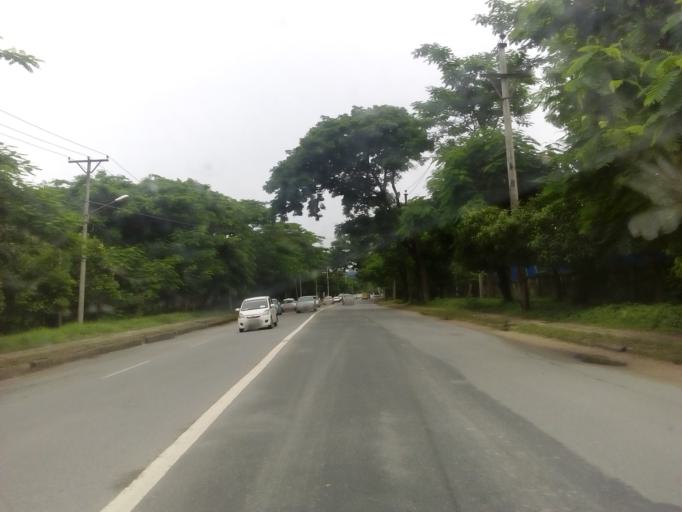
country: MM
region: Yangon
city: Yangon
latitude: 16.8559
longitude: 96.1339
